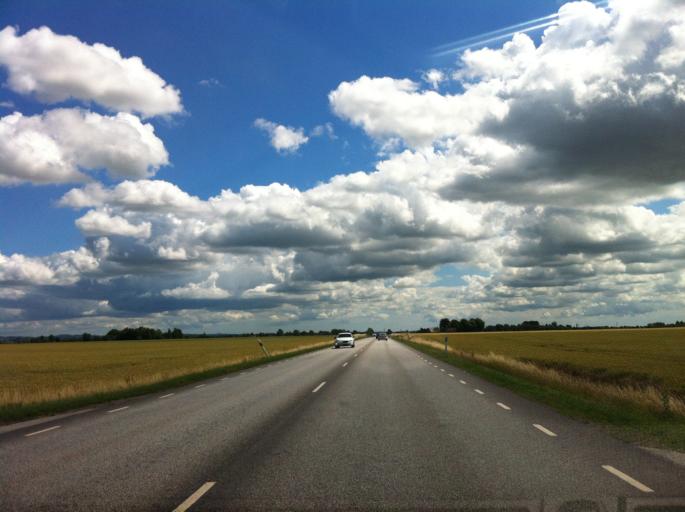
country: SE
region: Skane
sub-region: Staffanstorps Kommun
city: Hjaerup
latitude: 55.6820
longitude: 13.1636
